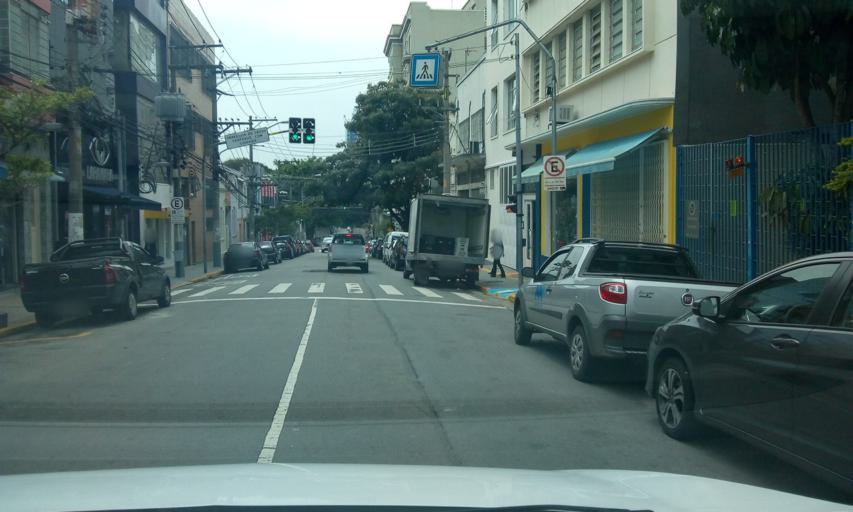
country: BR
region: Sao Paulo
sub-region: Sao Paulo
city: Sao Paulo
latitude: -23.5302
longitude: -46.6573
